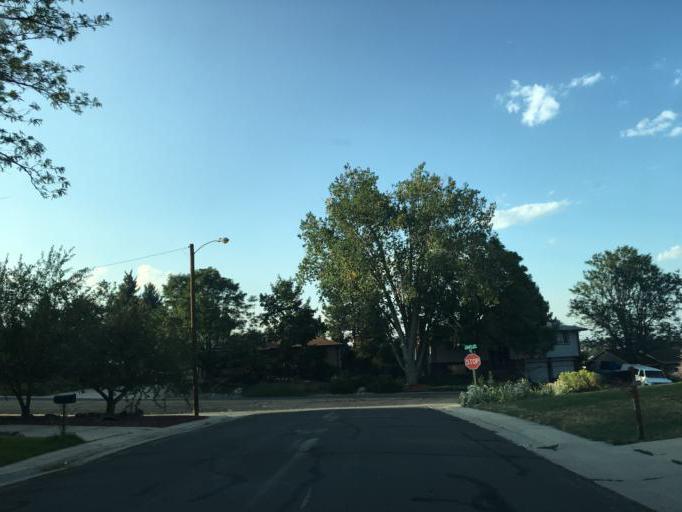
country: US
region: Colorado
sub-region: Jefferson County
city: Applewood
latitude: 39.7940
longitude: -105.1484
